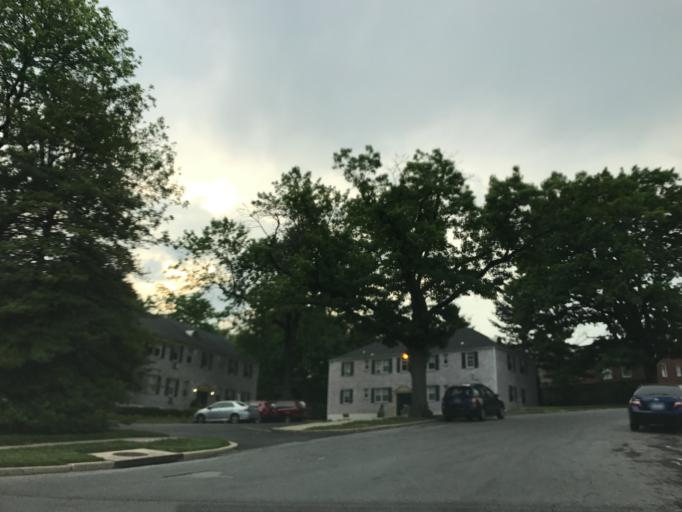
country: US
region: Maryland
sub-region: Baltimore County
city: Towson
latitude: 39.3729
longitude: -76.6058
